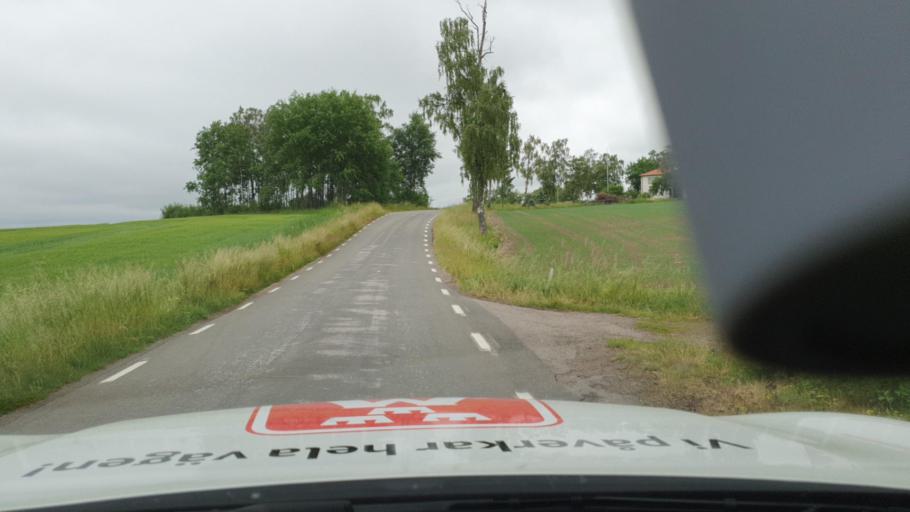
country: SE
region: Vaestra Goetaland
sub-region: Tidaholms Kommun
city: Olofstorp
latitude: 58.3840
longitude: 13.9989
